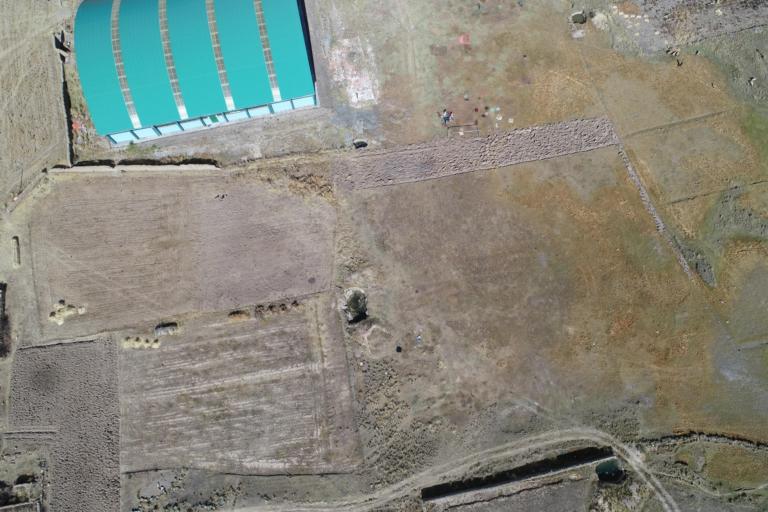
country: BO
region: La Paz
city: Achacachi
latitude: -15.8941
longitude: -68.9090
